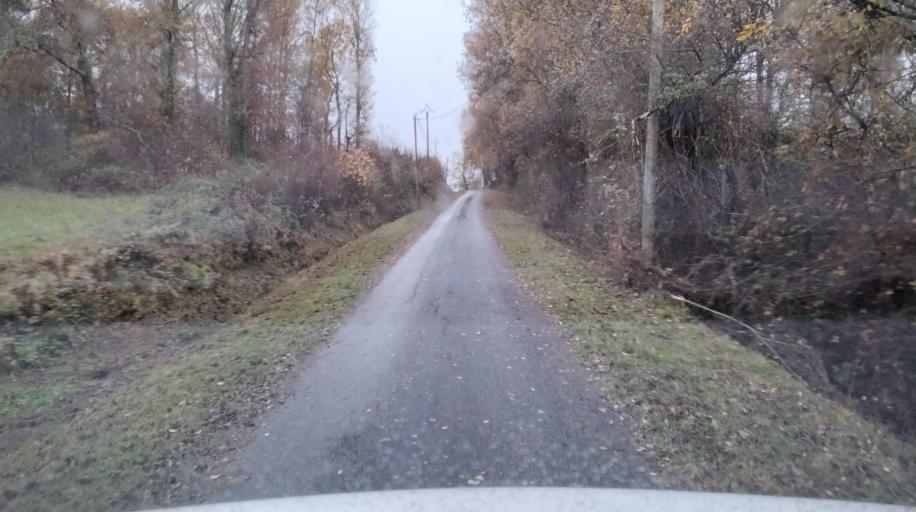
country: FR
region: Midi-Pyrenees
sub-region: Departement de la Haute-Garonne
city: Cazeres
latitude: 43.1665
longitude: 1.1449
